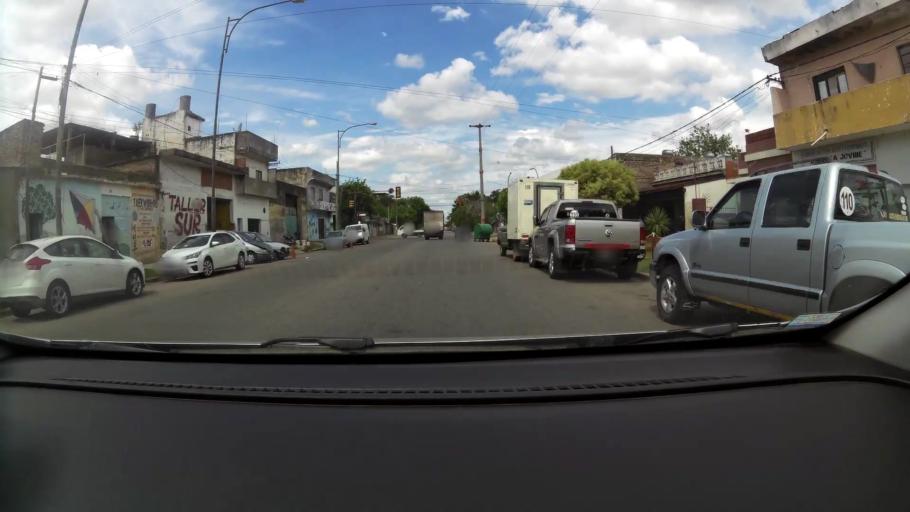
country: AR
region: Santa Fe
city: Gobernador Galvez
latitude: -33.0086
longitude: -60.6365
